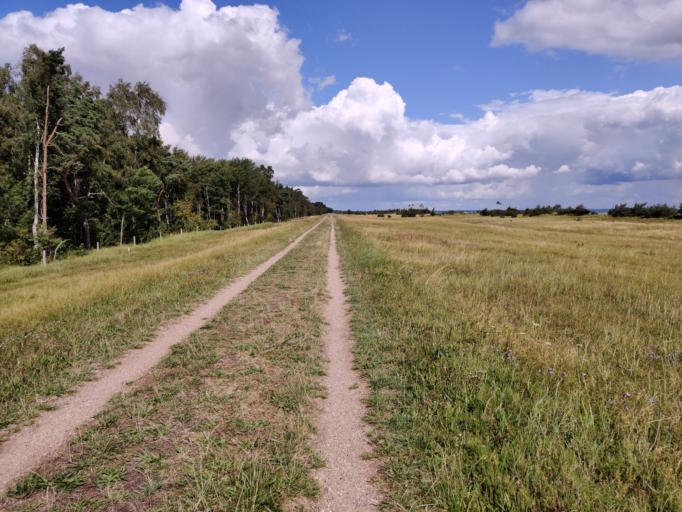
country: DK
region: Zealand
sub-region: Guldborgsund Kommune
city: Nykobing Falster
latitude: 54.6307
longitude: 11.9612
